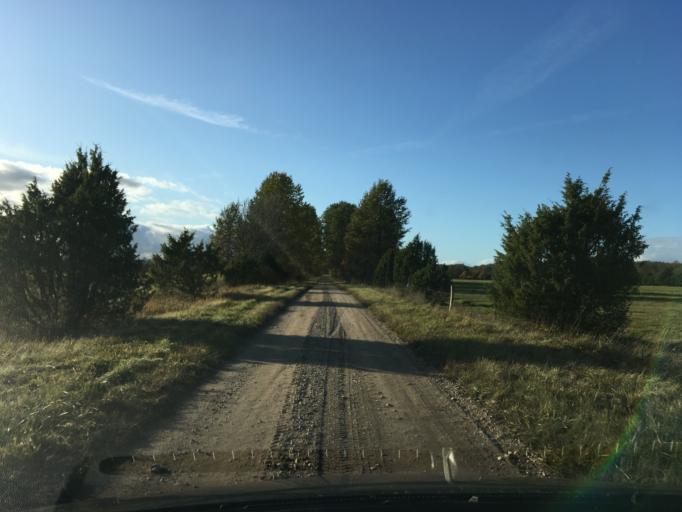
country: EE
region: Laeaene
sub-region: Lihula vald
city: Lihula
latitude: 58.5639
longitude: 23.7979
